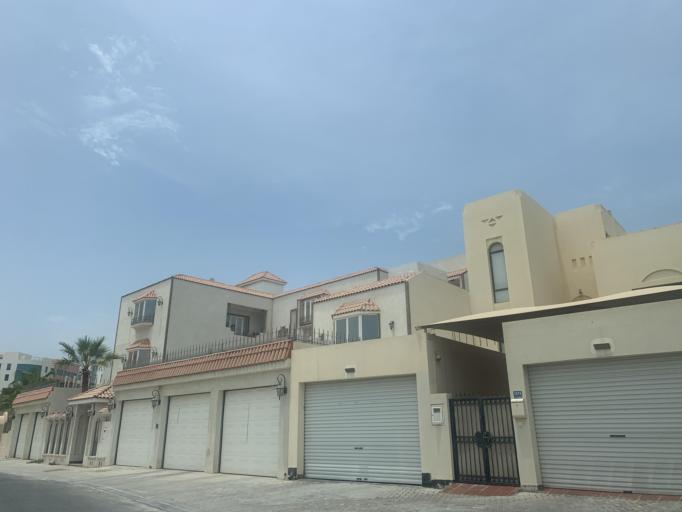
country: BH
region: Muharraq
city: Al Hadd
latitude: 26.2948
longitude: 50.6613
